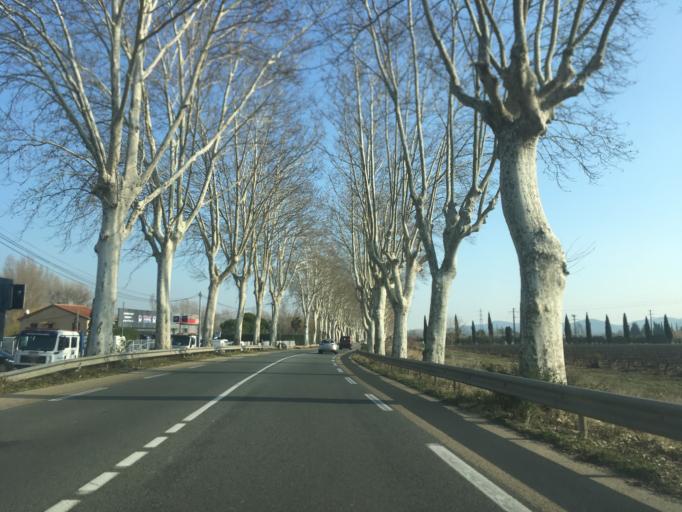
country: FR
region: Provence-Alpes-Cote d'Azur
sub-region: Departement du Var
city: Les Arcs
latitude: 43.4413
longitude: 6.4567
